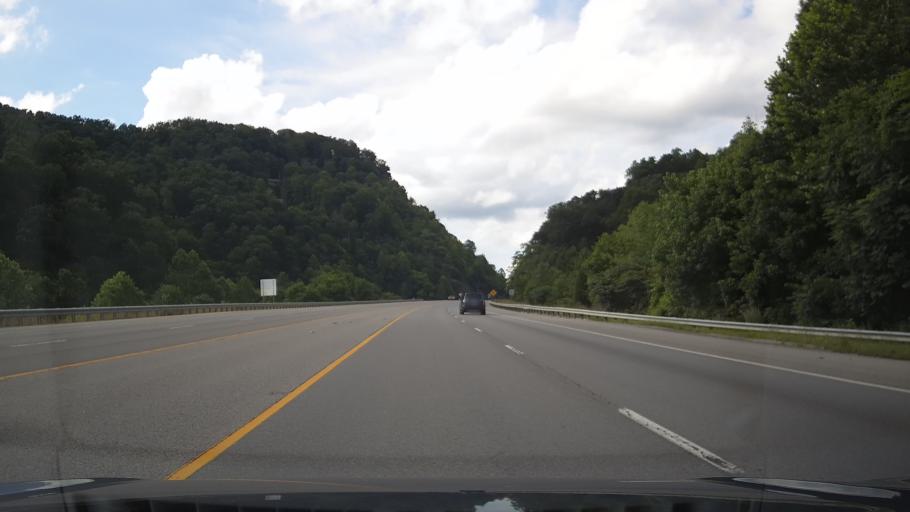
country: US
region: Kentucky
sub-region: Floyd County
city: Prestonsburg
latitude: 37.6898
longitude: -82.7908
